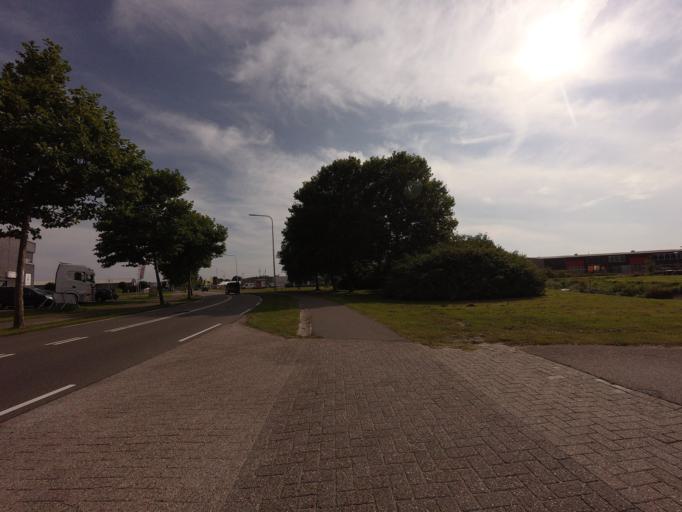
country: NL
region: Drenthe
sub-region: Gemeente Coevorden
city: Coevorden
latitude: 52.6658
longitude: 6.7239
